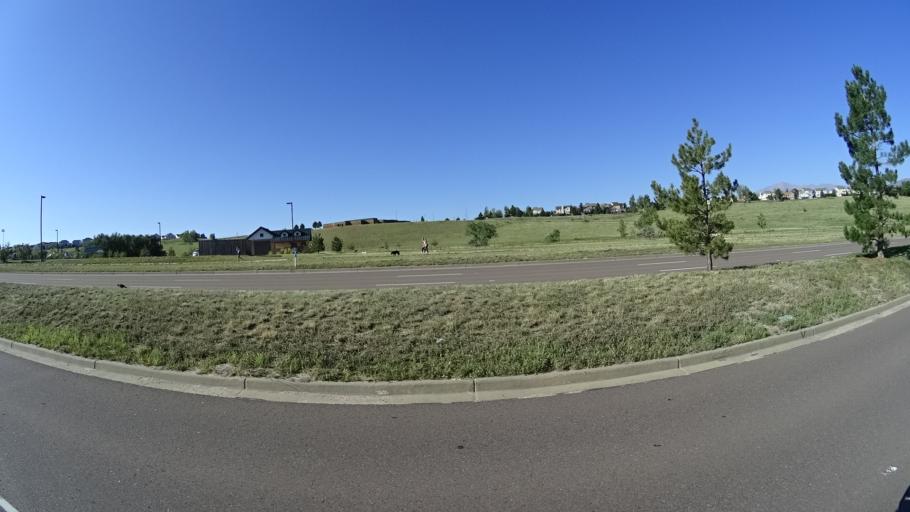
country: US
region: Colorado
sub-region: El Paso County
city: Black Forest
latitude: 38.9664
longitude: -104.7647
